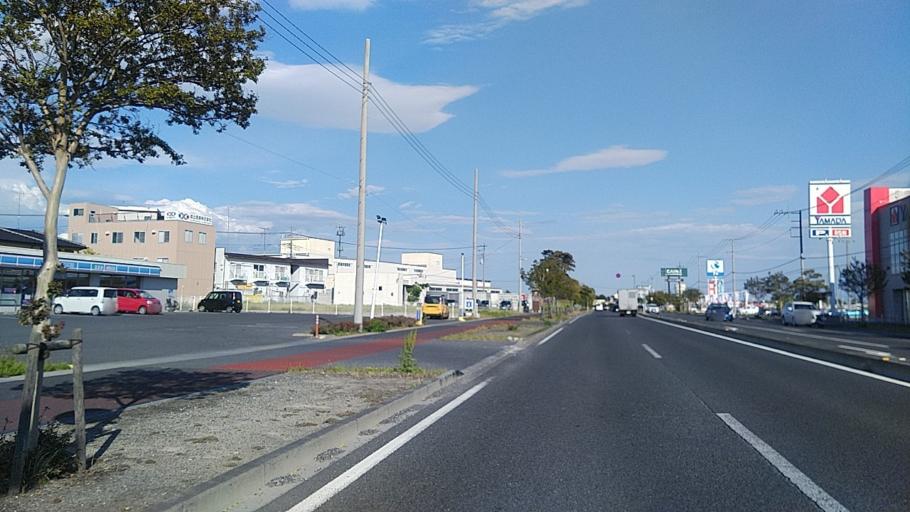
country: JP
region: Saitama
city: Menuma
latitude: 36.2660
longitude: 139.3987
